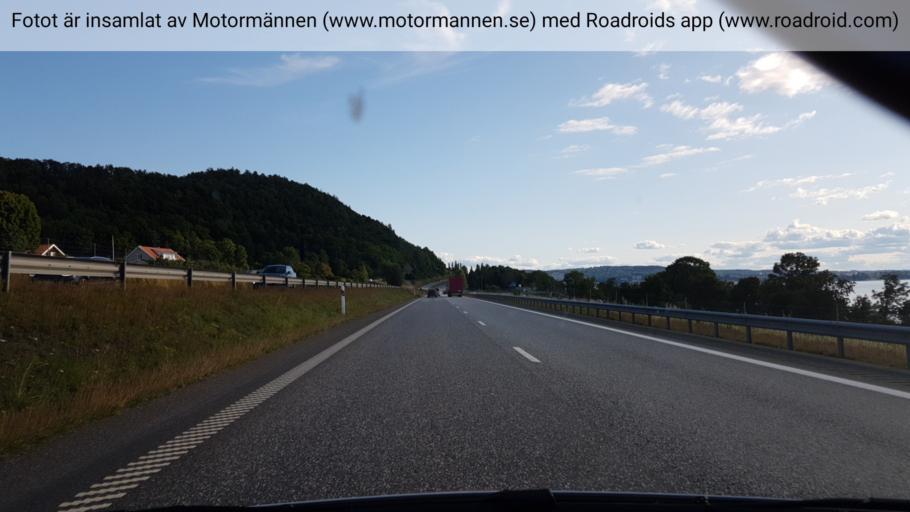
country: SE
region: Joenkoeping
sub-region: Jonkopings Kommun
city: Kaxholmen
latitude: 57.8358
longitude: 14.2693
